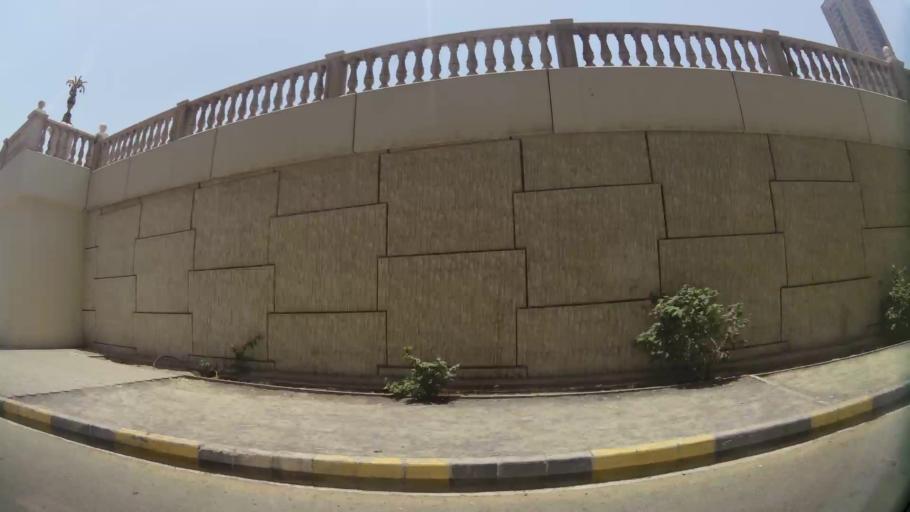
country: AE
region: Ash Shariqah
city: Sharjah
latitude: 25.3237
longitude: 55.3783
